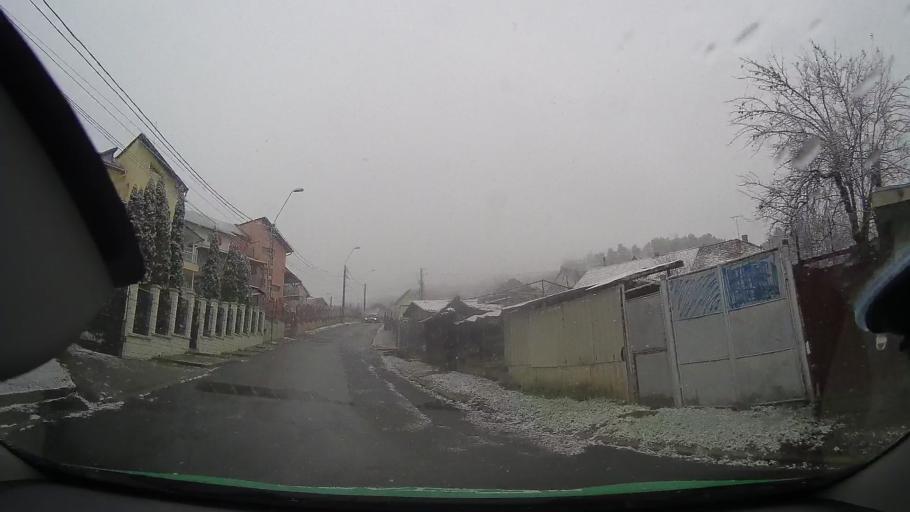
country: RO
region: Sibiu
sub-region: Municipiul Medias
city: Medias
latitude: 46.1616
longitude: 24.3646
